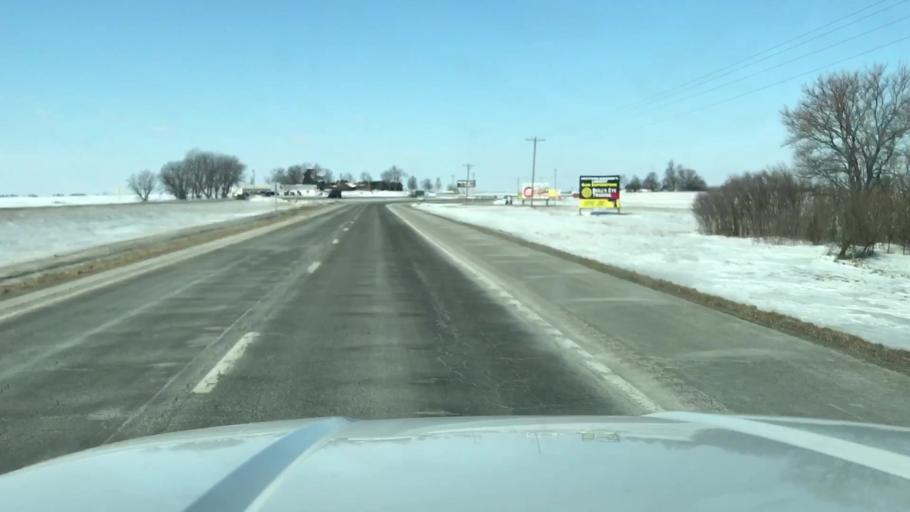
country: US
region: Missouri
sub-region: Nodaway County
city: Maryville
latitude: 40.2755
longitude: -94.8713
